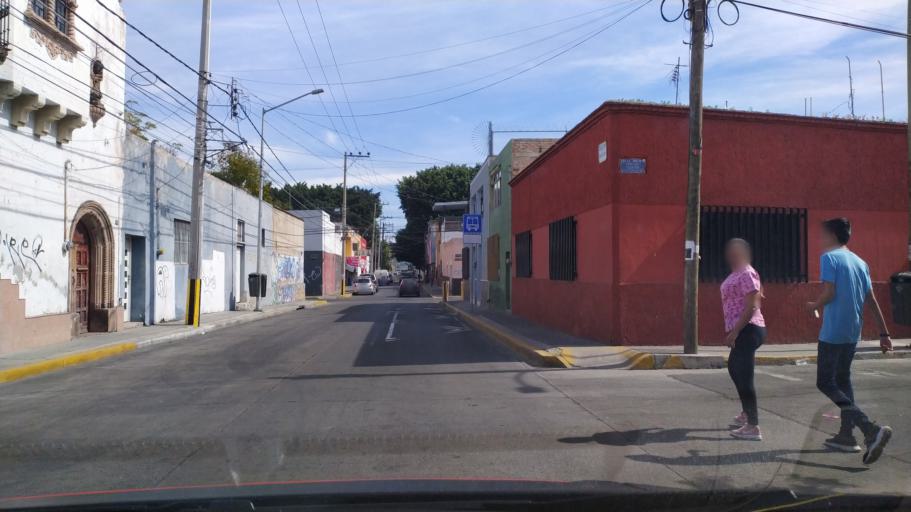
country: MX
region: Jalisco
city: Tlaquepaque
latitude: 20.6821
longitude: -103.3318
